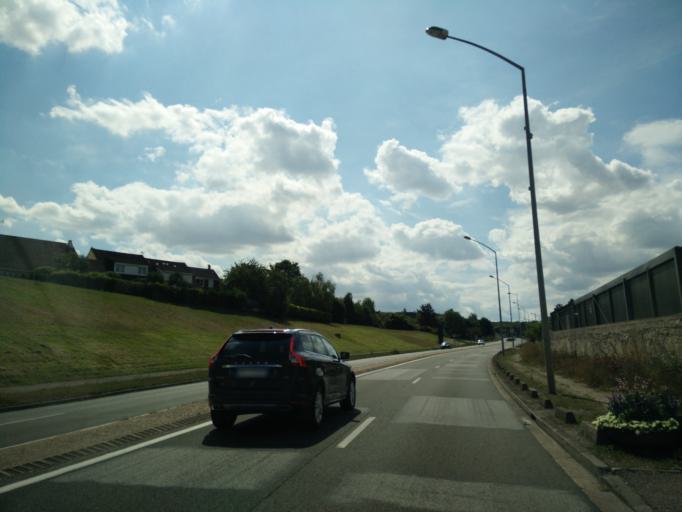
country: FR
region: Ile-de-France
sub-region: Departement des Yvelines
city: Mantes-la-Jolie
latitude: 48.9718
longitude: 1.7170
